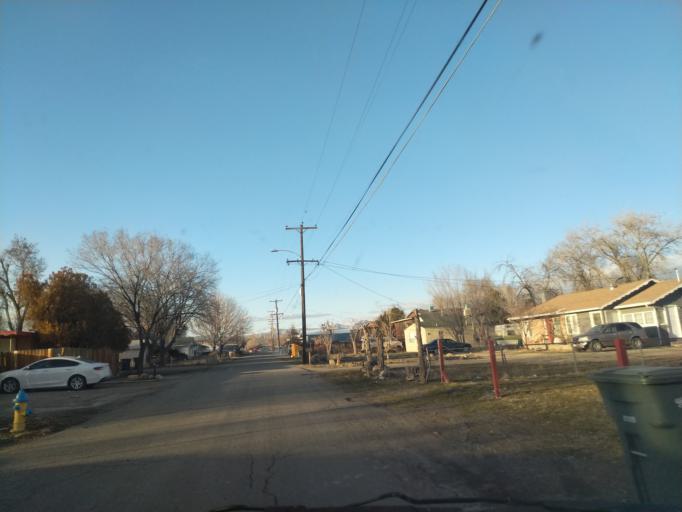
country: US
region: Colorado
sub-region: Mesa County
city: Fruitvale
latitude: 39.0754
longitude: -108.5210
